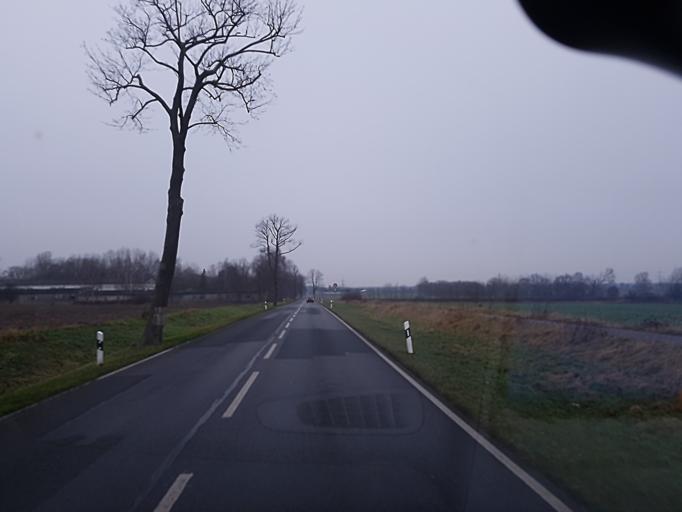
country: DE
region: Brandenburg
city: Lubbenau
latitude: 51.8741
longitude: 13.9129
